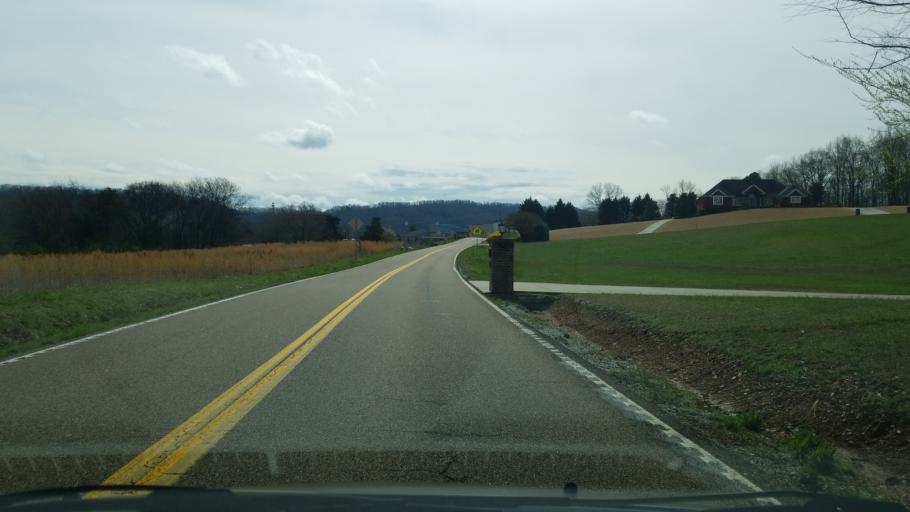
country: US
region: Tennessee
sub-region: Hamilton County
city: Collegedale
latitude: 35.0976
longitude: -85.0645
